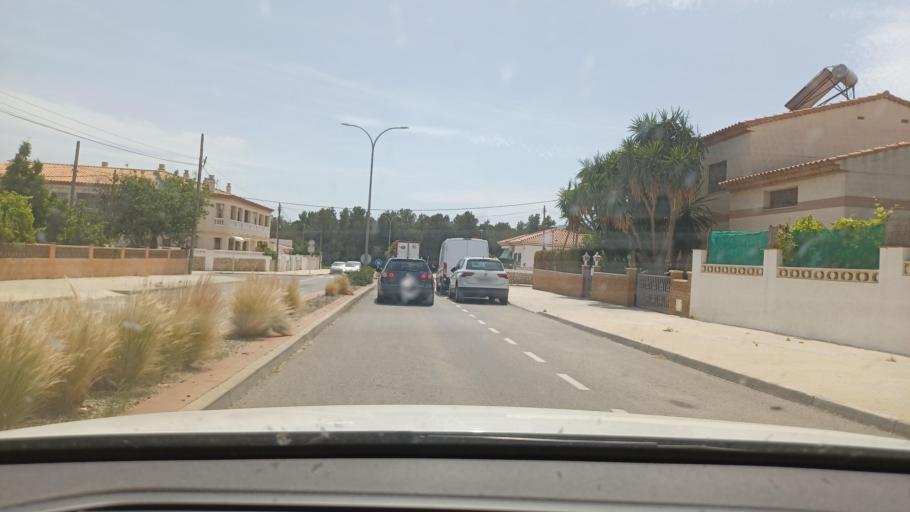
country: ES
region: Catalonia
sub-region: Provincia de Tarragona
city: Colldejou
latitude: 41.0046
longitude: 0.9267
